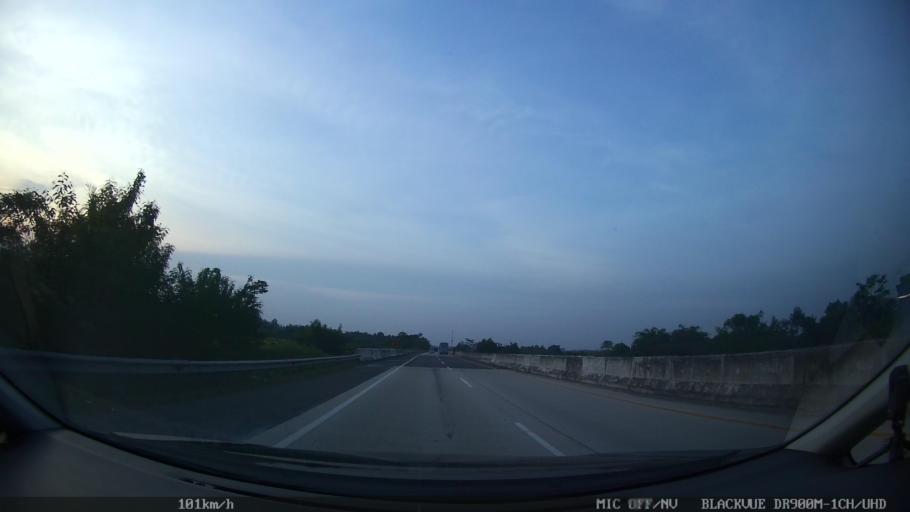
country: ID
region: Lampung
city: Penengahan
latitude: -5.7737
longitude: 105.7170
